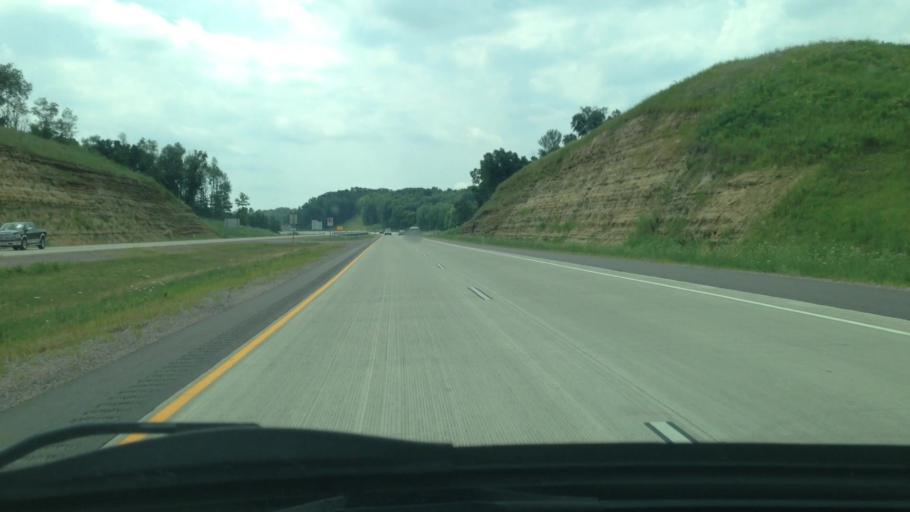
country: US
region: Wisconsin
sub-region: Sauk County
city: West Baraboo
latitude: 43.4412
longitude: -89.7785
